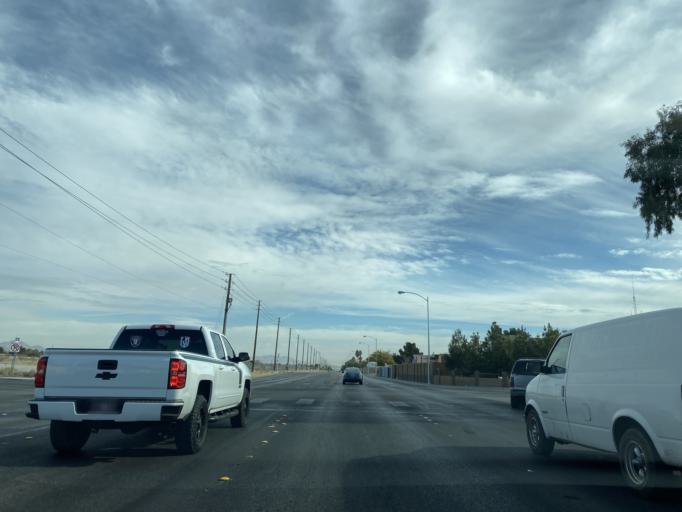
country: US
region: Nevada
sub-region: Clark County
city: North Las Vegas
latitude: 36.2467
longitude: -115.1990
